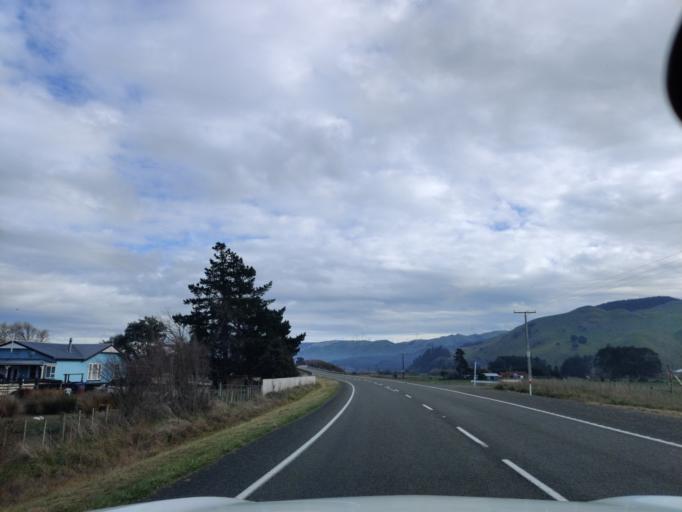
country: NZ
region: Manawatu-Wanganui
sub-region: Palmerston North City
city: Palmerston North
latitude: -40.3335
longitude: 175.8458
